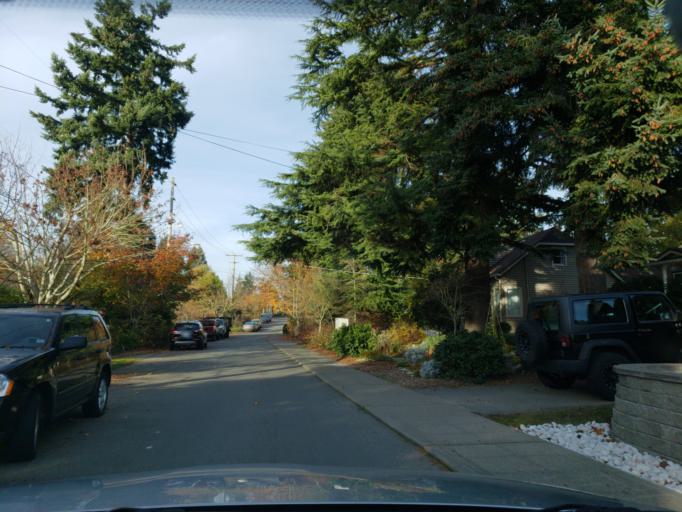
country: US
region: Washington
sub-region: King County
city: Shoreline
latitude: 47.7073
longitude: -122.3581
